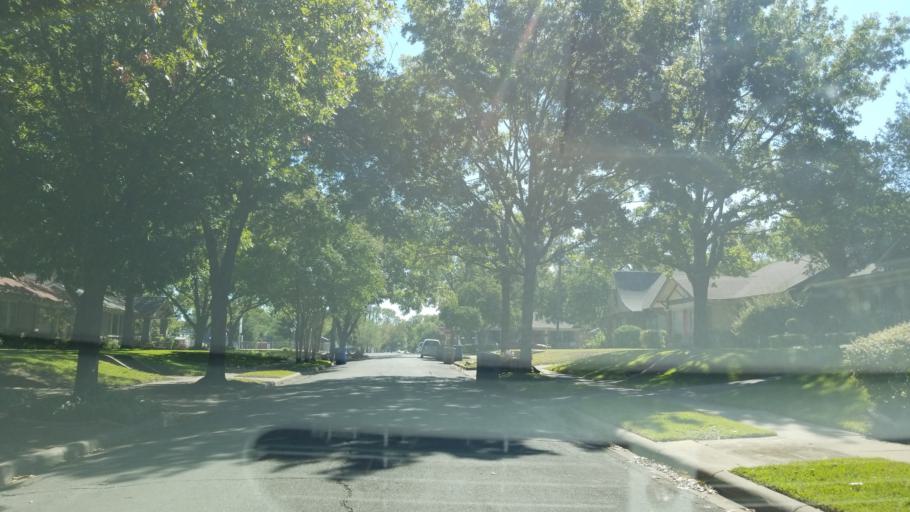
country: US
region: Texas
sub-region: Dallas County
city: Highland Park
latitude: 32.8075
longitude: -96.7587
